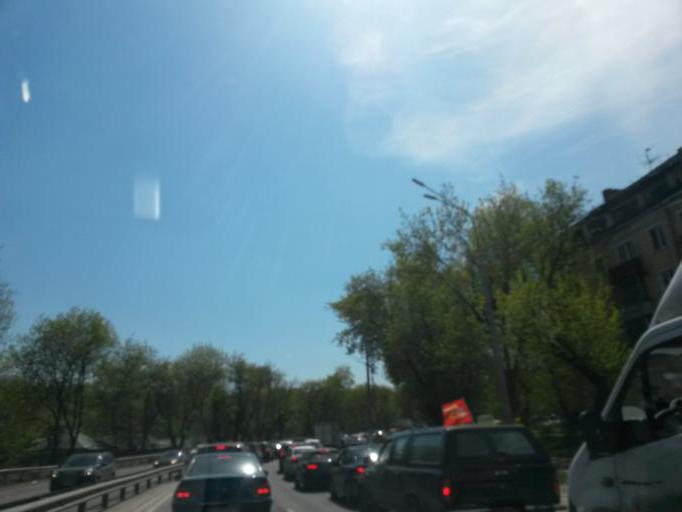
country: RU
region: Moskovskaya
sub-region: Podol'skiy Rayon
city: Podol'sk
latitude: 55.4398
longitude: 37.5564
